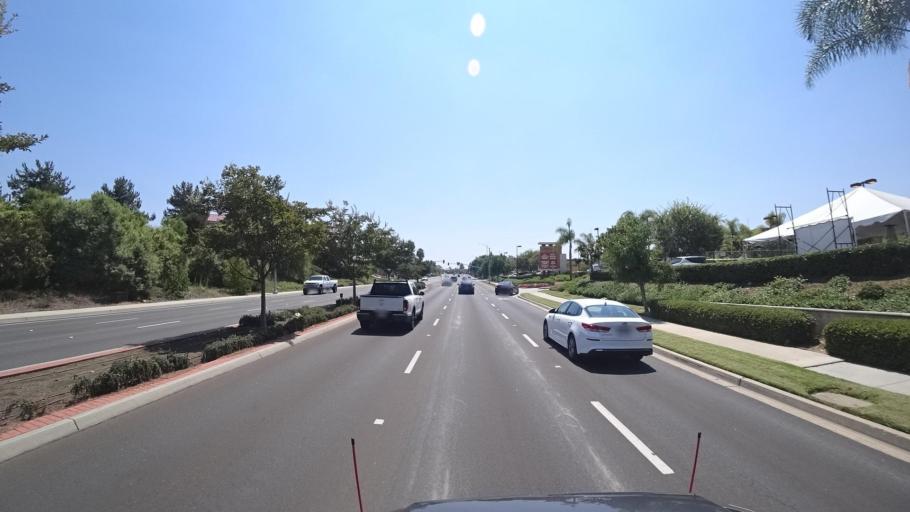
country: US
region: California
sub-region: San Diego County
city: Vista
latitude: 33.1894
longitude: -117.2539
